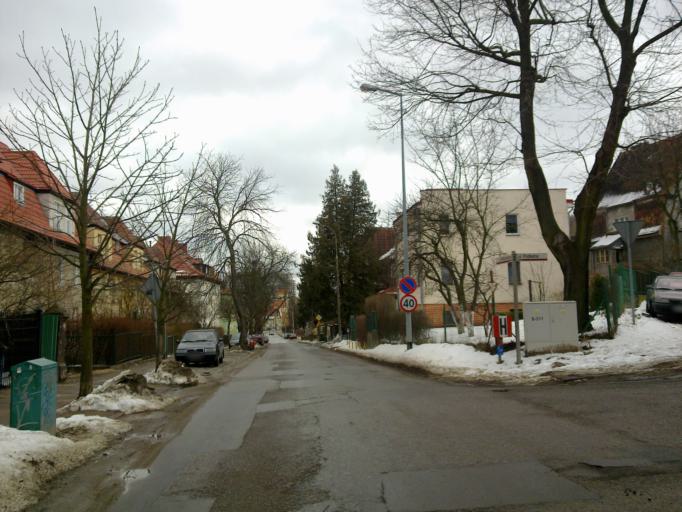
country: PL
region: Pomeranian Voivodeship
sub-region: Gdansk
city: Gdansk
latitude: 54.3783
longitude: 18.5942
